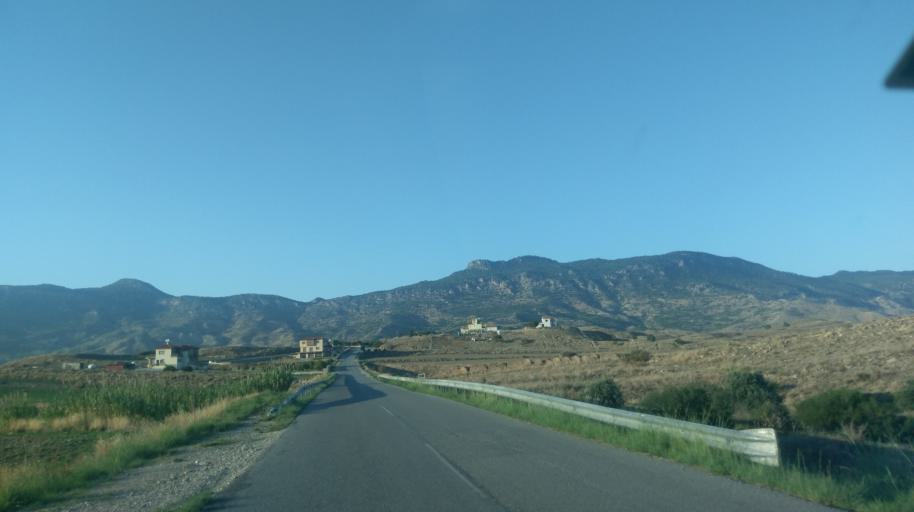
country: CY
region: Ammochostos
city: Lefkonoiko
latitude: 35.2498
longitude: 33.5511
